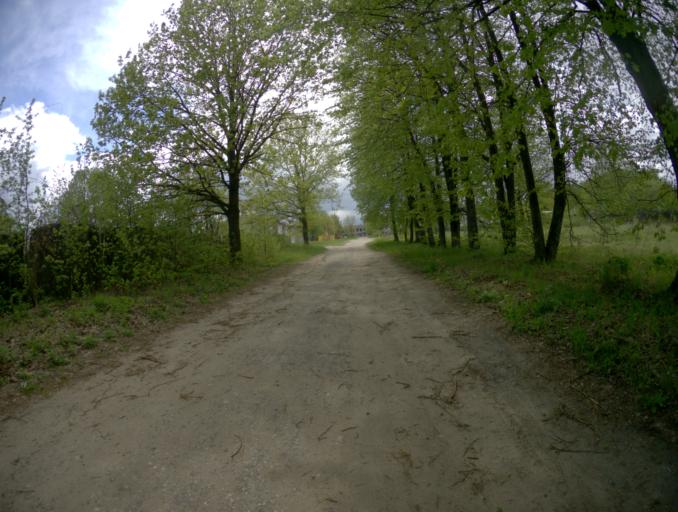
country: RU
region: Vladimir
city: Velikodvorskiy
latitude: 55.2399
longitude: 40.6550
